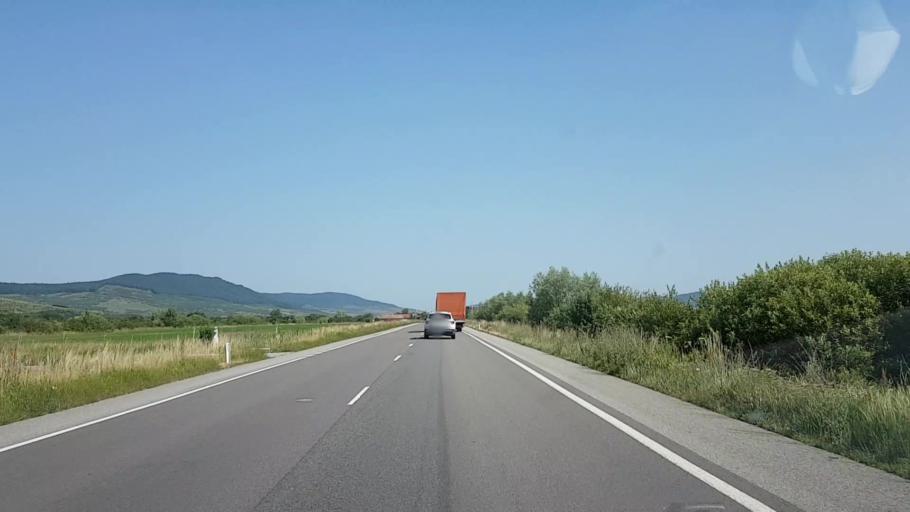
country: RO
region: Bistrita-Nasaud
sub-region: Comuna Sieu-Odorhei
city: Sieu-Odorhei
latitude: 47.1212
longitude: 24.3271
